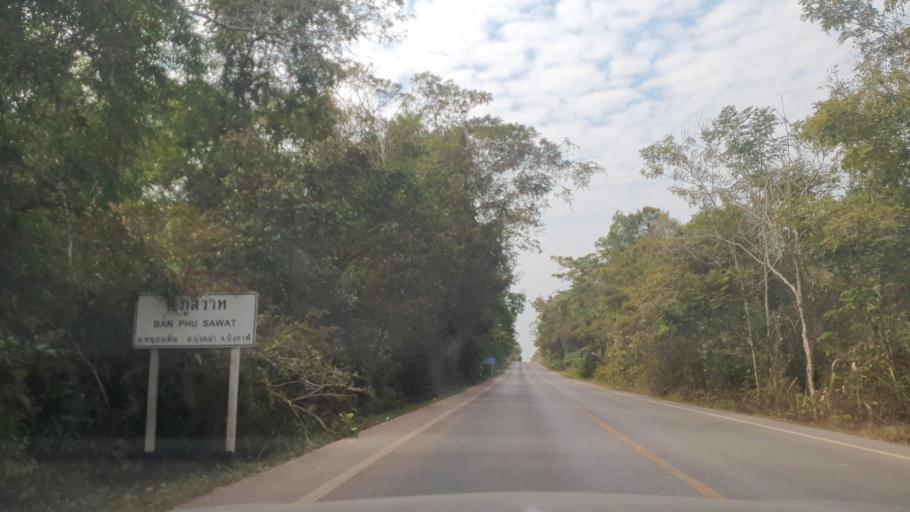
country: TH
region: Changwat Bueng Kan
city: Bung Khla
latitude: 18.2912
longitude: 103.9137
